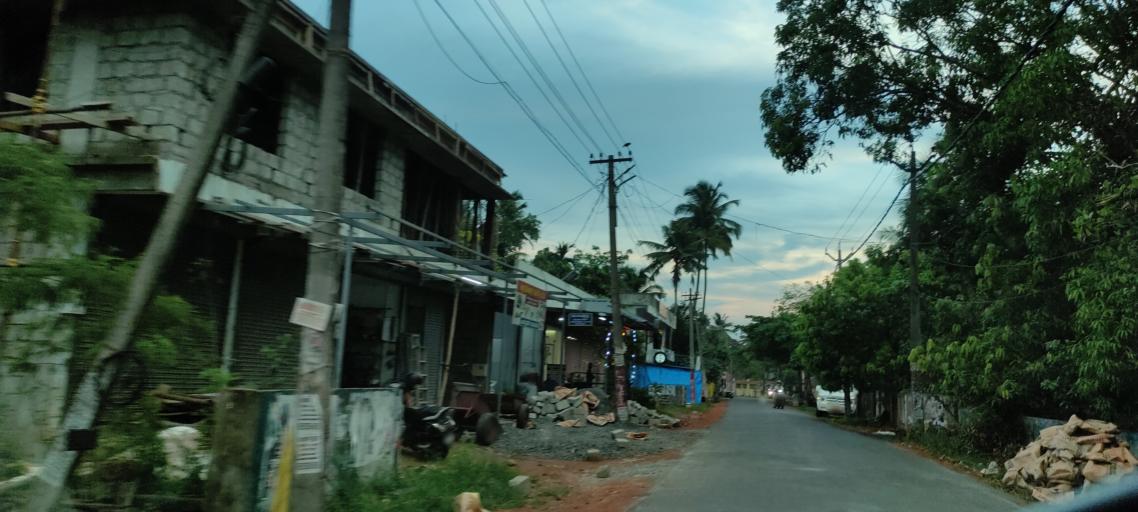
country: IN
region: Kerala
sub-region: Alappuzha
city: Shertallai
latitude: 9.6981
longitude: 76.3504
